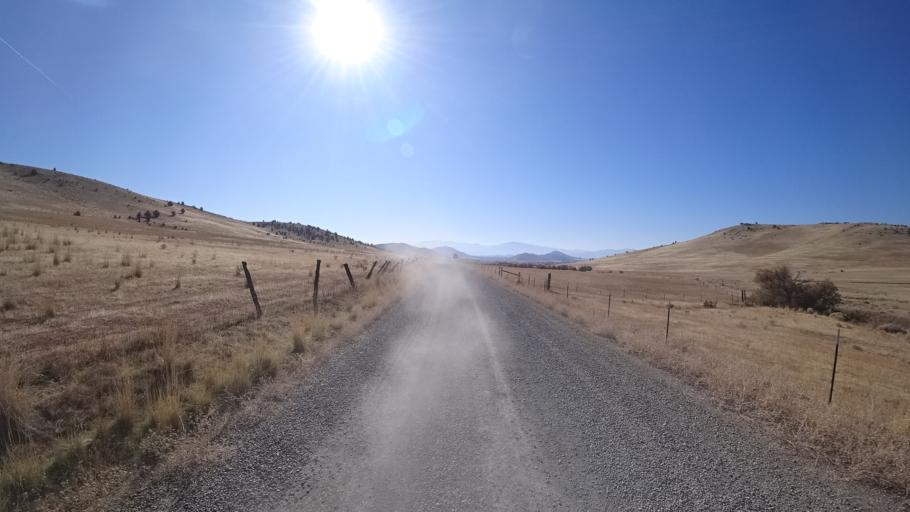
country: US
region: California
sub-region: Siskiyou County
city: Montague
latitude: 41.7407
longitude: -122.3671
